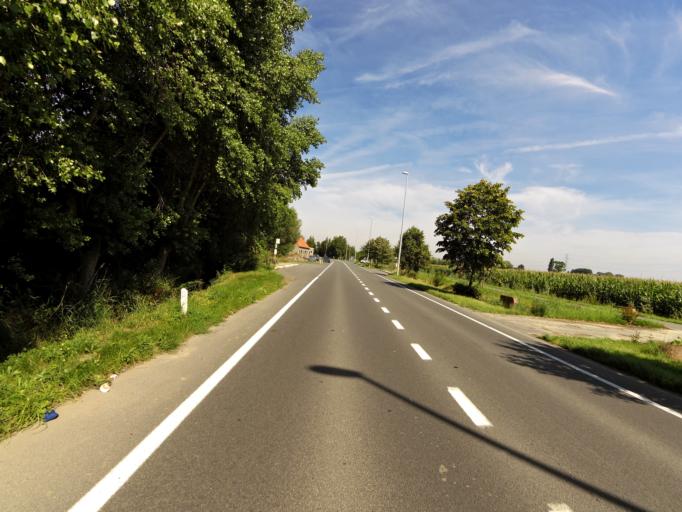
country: BE
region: Flanders
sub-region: Provincie West-Vlaanderen
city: Zuienkerke
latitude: 51.2325
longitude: 3.1842
